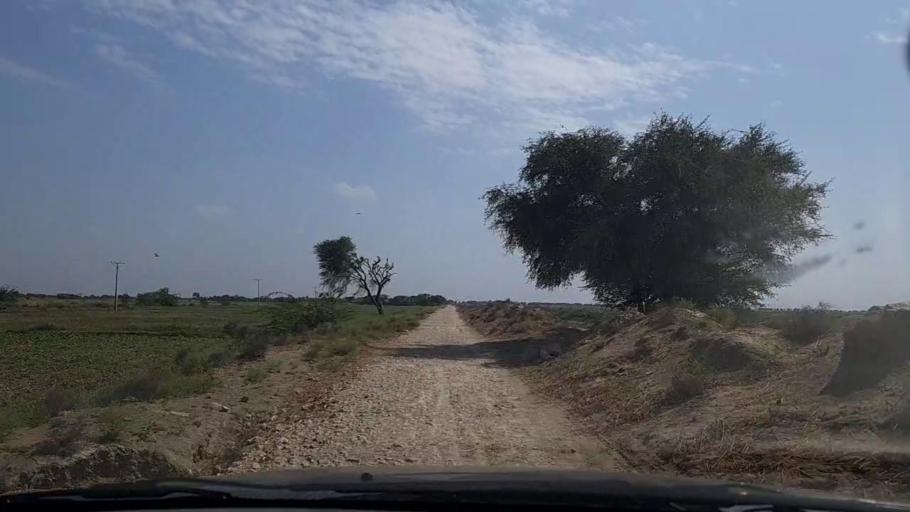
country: PK
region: Sindh
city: Mirpur Batoro
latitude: 24.5785
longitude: 68.1959
